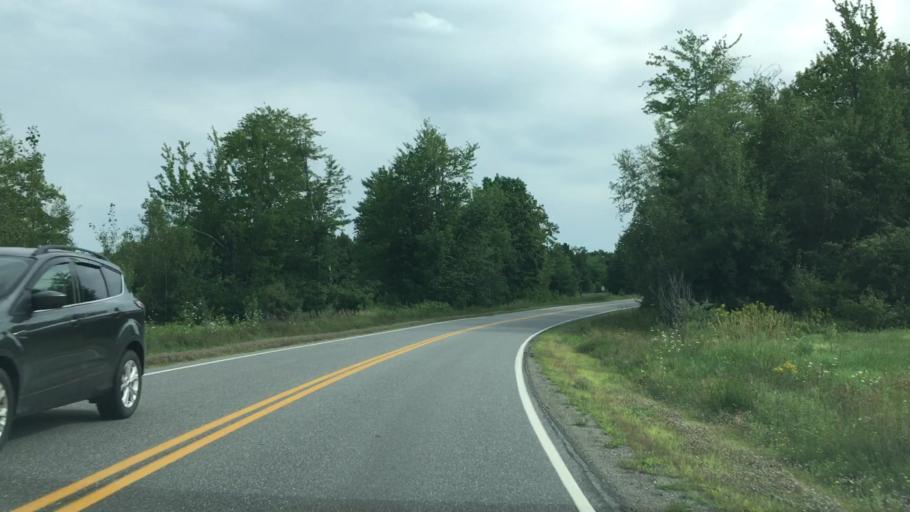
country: US
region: Maine
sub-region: Waldo County
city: Belfast
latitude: 44.3752
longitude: -69.0315
